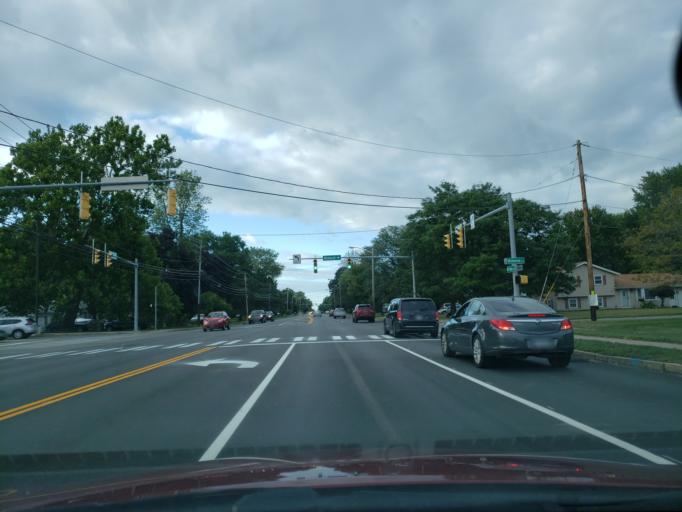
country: US
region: New York
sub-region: Monroe County
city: Greece
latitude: 43.2277
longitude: -77.6590
